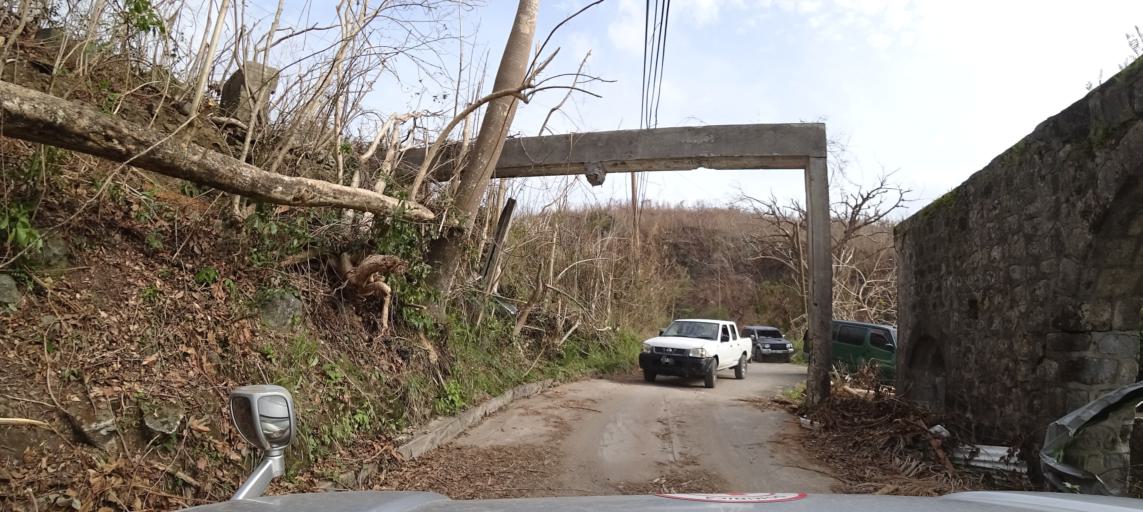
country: DM
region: Saint George
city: Roseau
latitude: 15.3273
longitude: -61.3865
